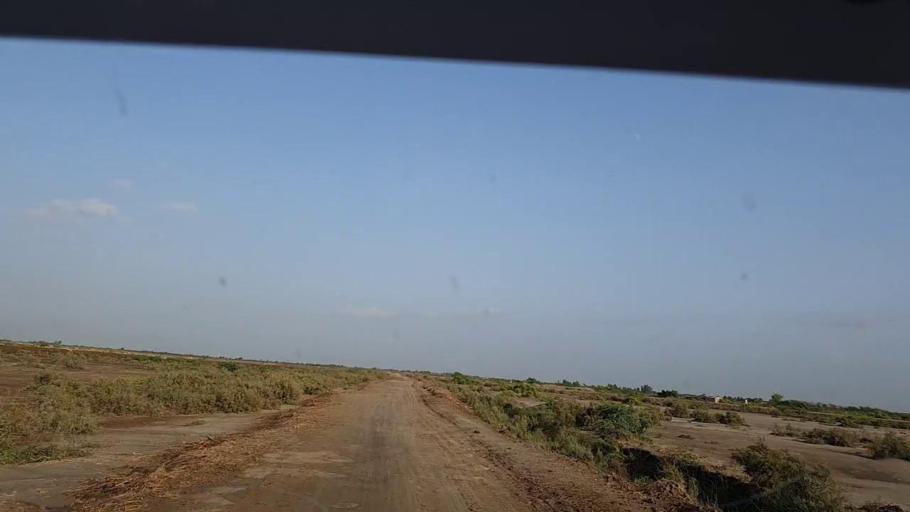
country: PK
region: Sindh
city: Badin
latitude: 24.5510
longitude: 68.8742
